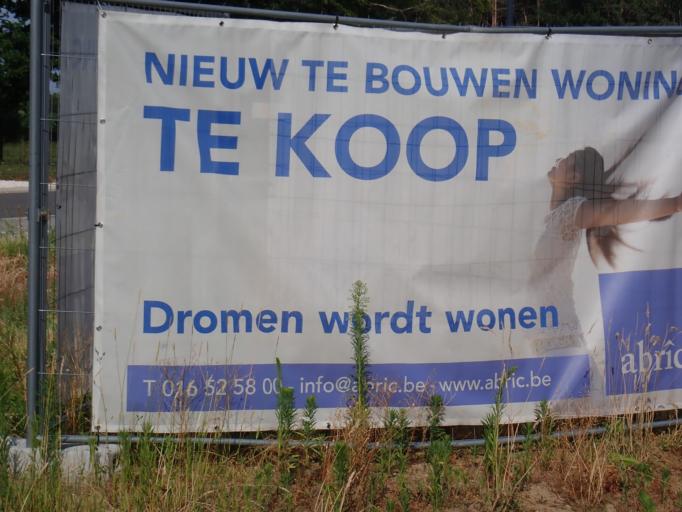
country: BE
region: Flanders
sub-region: Provincie Vlaams-Brabant
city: Keerbergen
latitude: 51.0094
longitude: 4.6298
